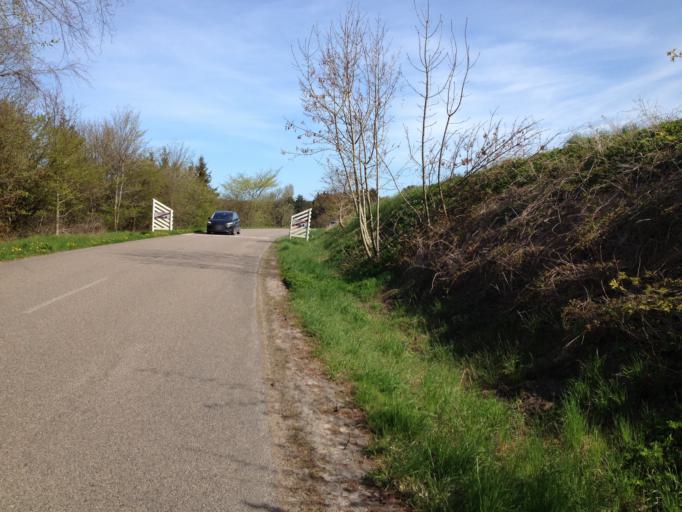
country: DK
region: Capital Region
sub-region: Halsnaes Kommune
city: Hundested
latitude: 55.9521
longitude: 11.8990
